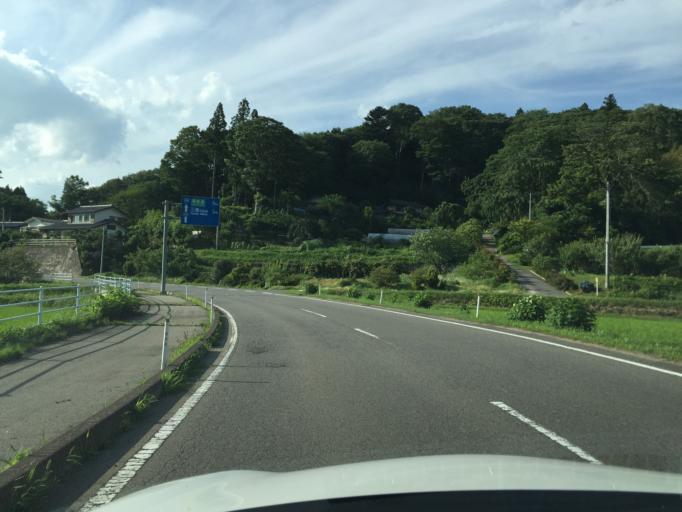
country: JP
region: Fukushima
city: Miharu
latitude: 37.4045
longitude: 140.5031
